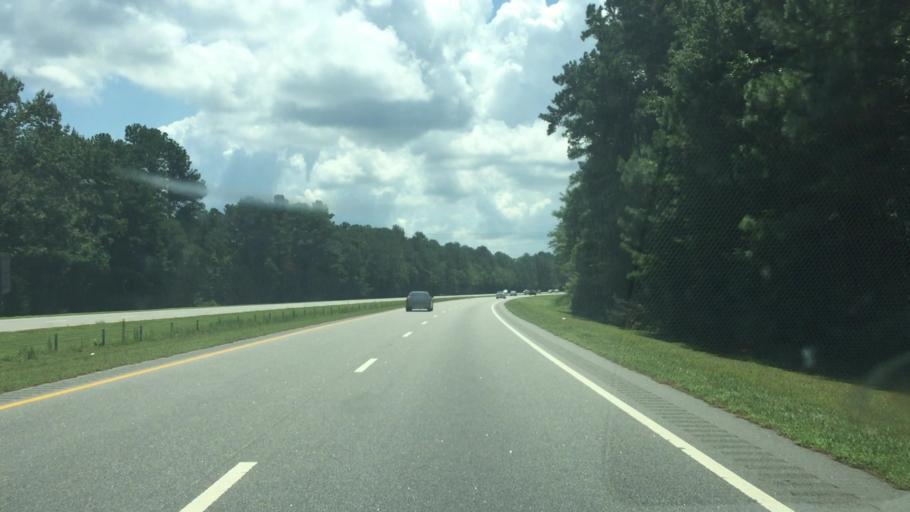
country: US
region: North Carolina
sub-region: Robeson County
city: Lumberton
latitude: 34.5686
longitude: -79.0306
